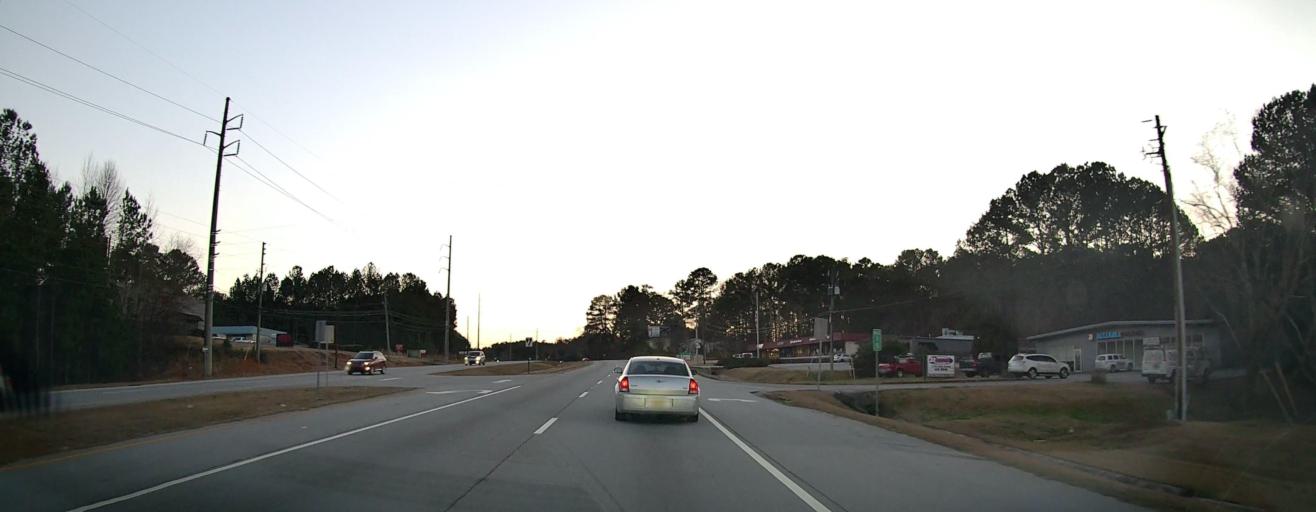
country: US
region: Georgia
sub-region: Clayton County
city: Riverdale
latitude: 33.5155
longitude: -84.4286
